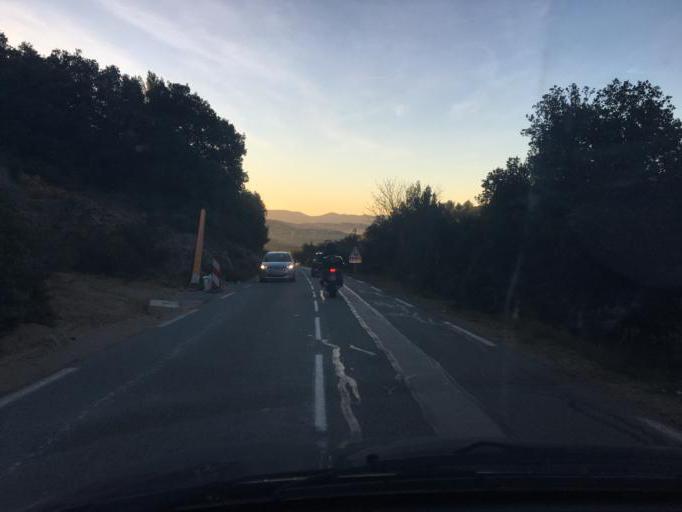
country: FR
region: Provence-Alpes-Cote d'Azur
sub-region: Departement du Var
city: Taradeau
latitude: 43.4590
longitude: 6.4194
